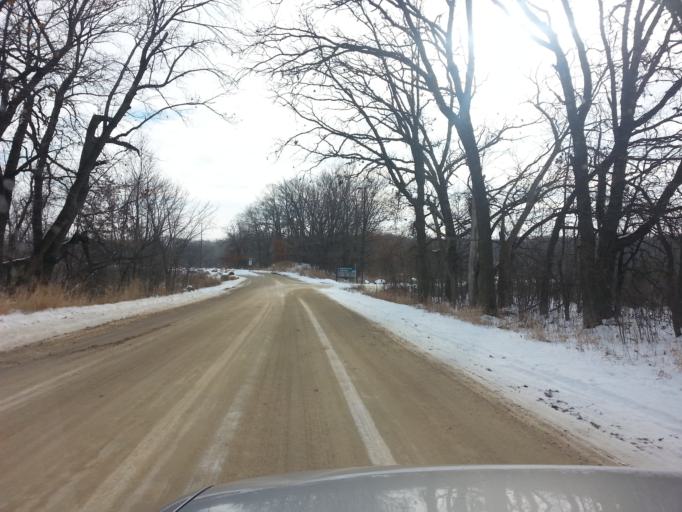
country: US
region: Minnesota
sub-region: Scott County
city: Prior Lake
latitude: 44.7173
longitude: -93.4734
